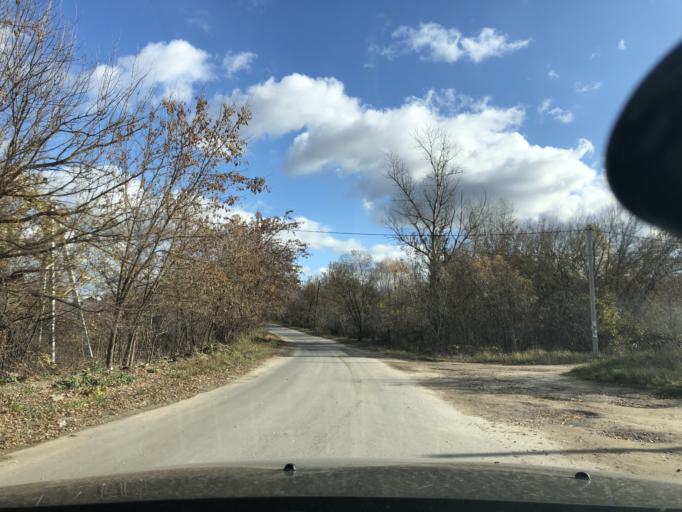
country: RU
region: Tula
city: Gorelki
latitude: 54.2950
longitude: 37.5604
